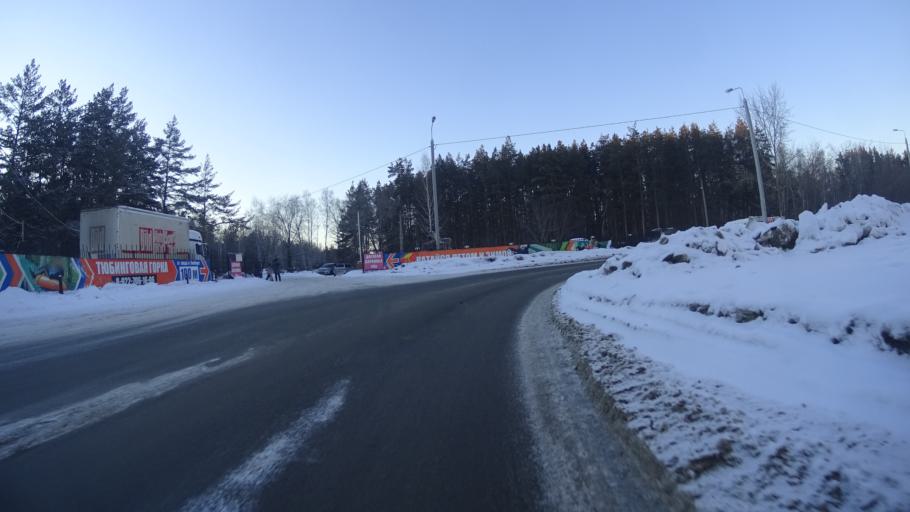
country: RU
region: Chelyabinsk
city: Roshchino
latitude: 55.1964
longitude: 61.2984
